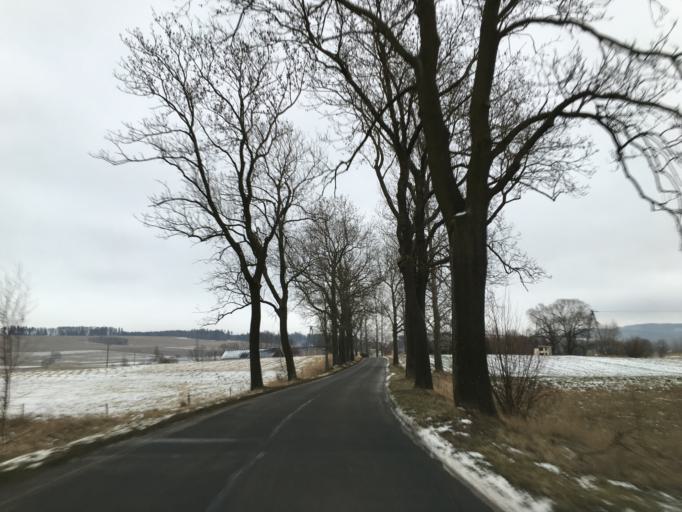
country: PL
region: Lower Silesian Voivodeship
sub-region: Powiat kamiennogorski
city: Krzeszow
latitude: 50.7085
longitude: 16.1071
